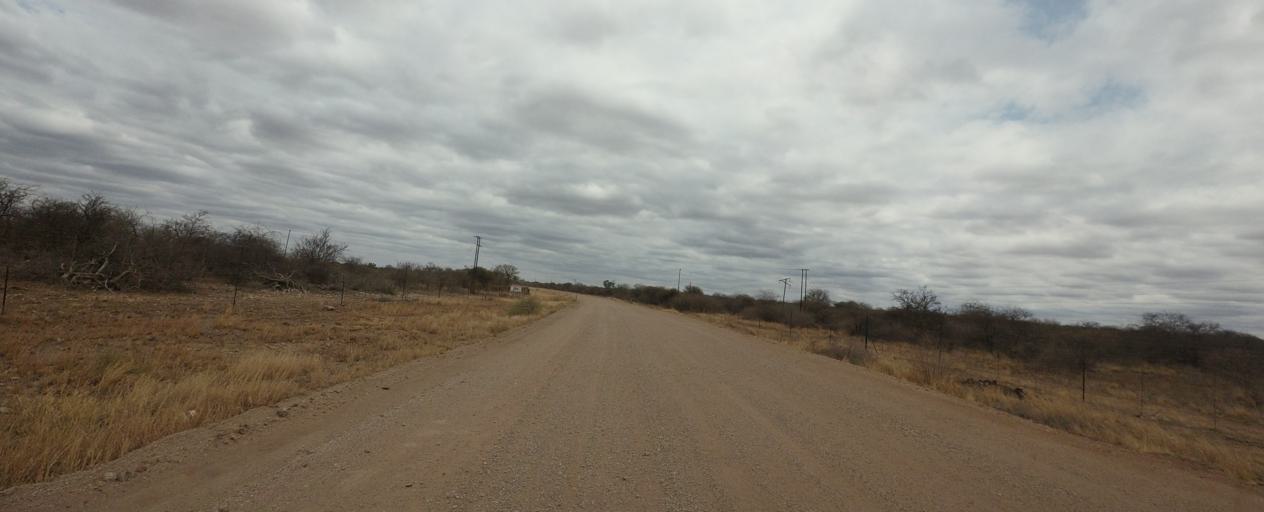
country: BW
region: Central
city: Mathathane
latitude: -22.7113
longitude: 28.5647
